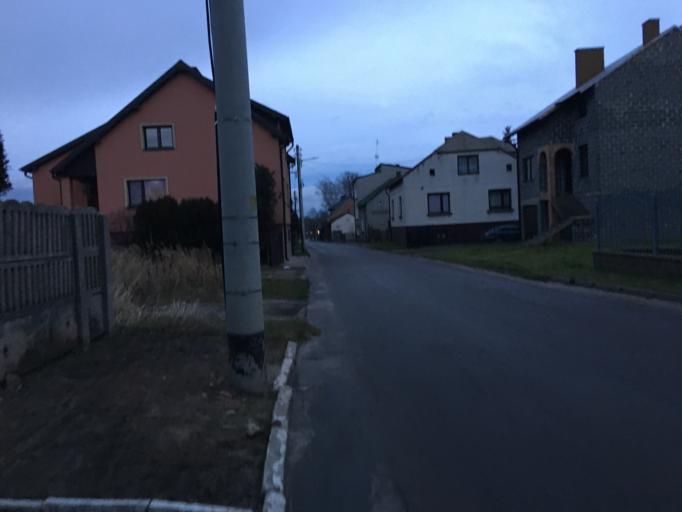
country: PL
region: Silesian Voivodeship
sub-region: Powiat myszkowski
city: Myszkow
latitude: 50.5435
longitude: 19.3661
